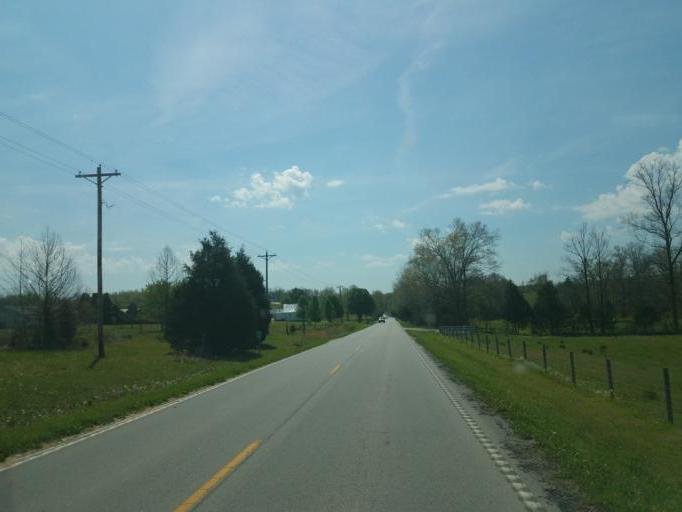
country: US
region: Kentucky
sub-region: Edmonson County
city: Brownsville
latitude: 37.1763
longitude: -86.4261
